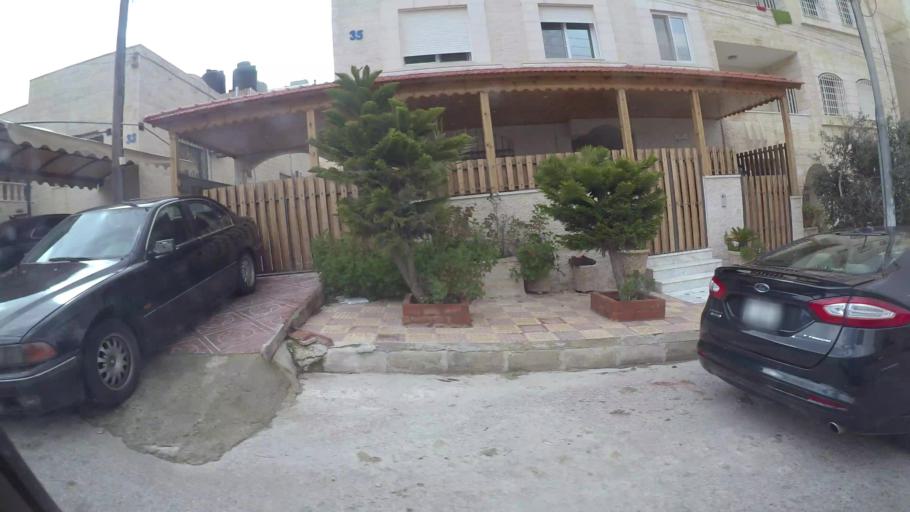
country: JO
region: Amman
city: Al Jubayhah
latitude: 32.0673
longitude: 35.8823
